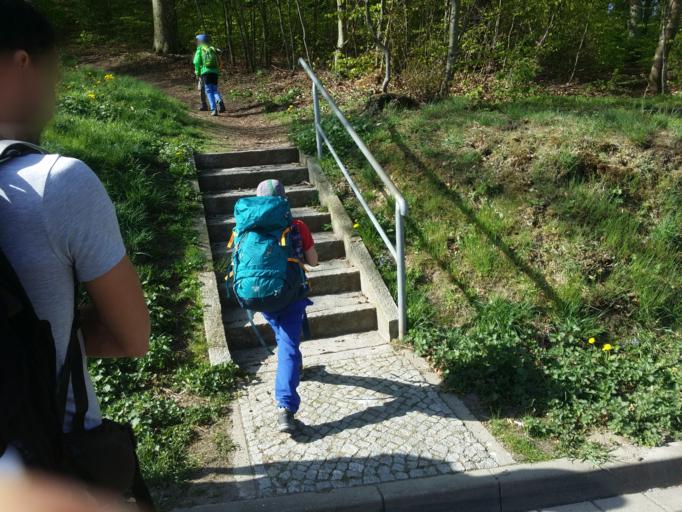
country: DE
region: Saxony-Anhalt
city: Bad Suderode
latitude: 51.7257
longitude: 11.1204
